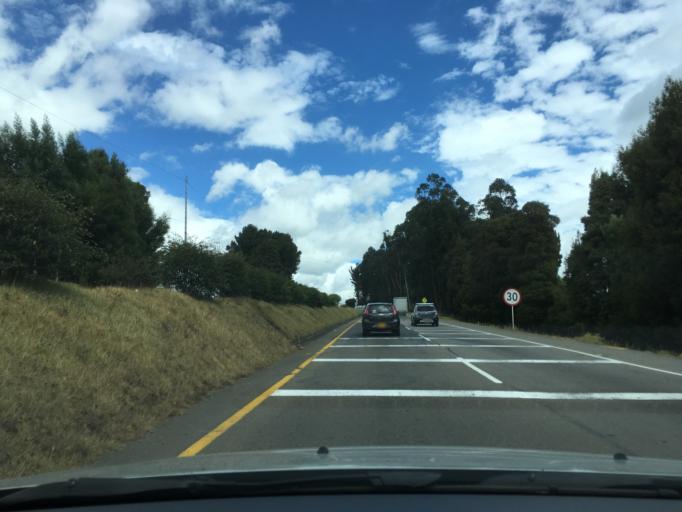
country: CO
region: Boyaca
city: Tuta
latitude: 5.6695
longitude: -73.2697
